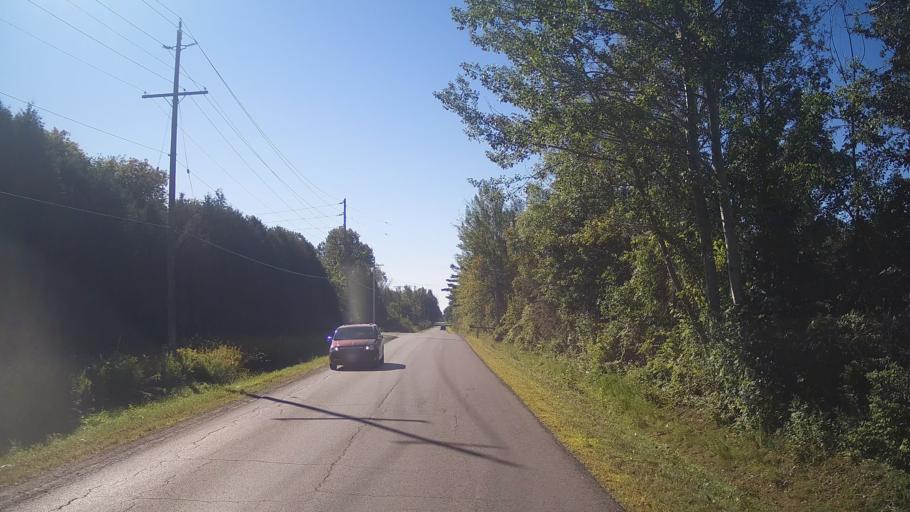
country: CA
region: Ontario
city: Prescott
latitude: 45.0182
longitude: -75.6164
